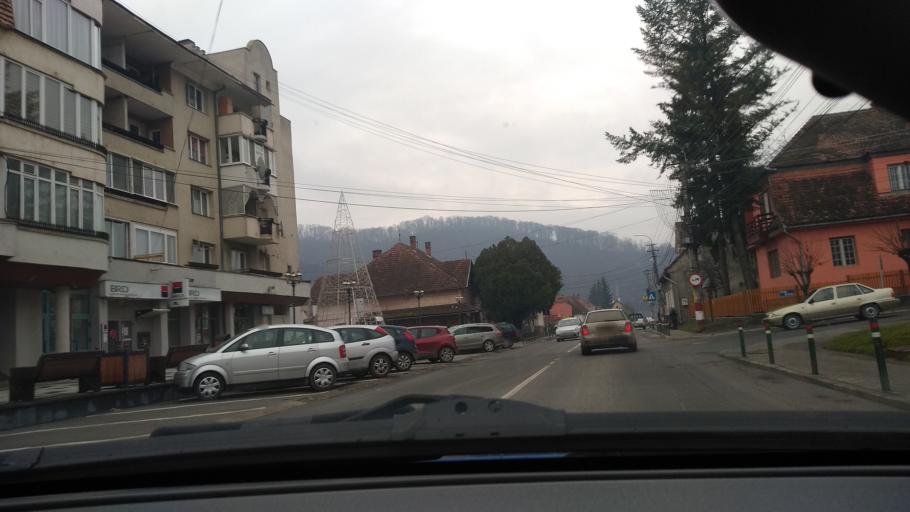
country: RO
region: Mures
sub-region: Oras Sovata
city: Sovata
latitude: 46.5970
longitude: 25.0710
